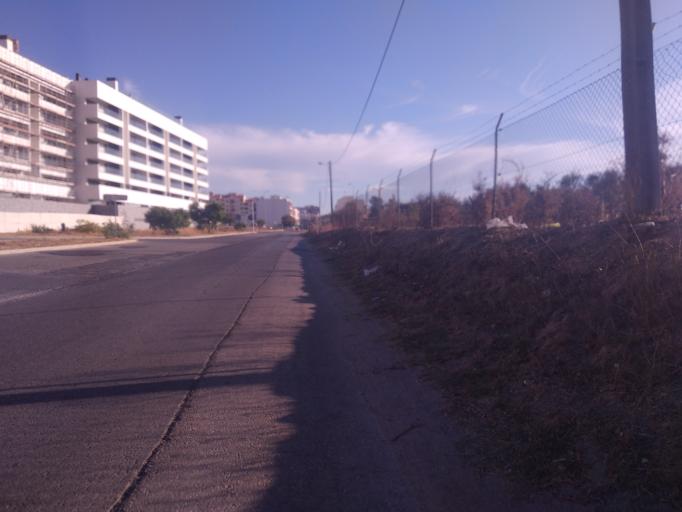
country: PT
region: Faro
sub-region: Faro
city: Faro
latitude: 37.0311
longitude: -7.9399
